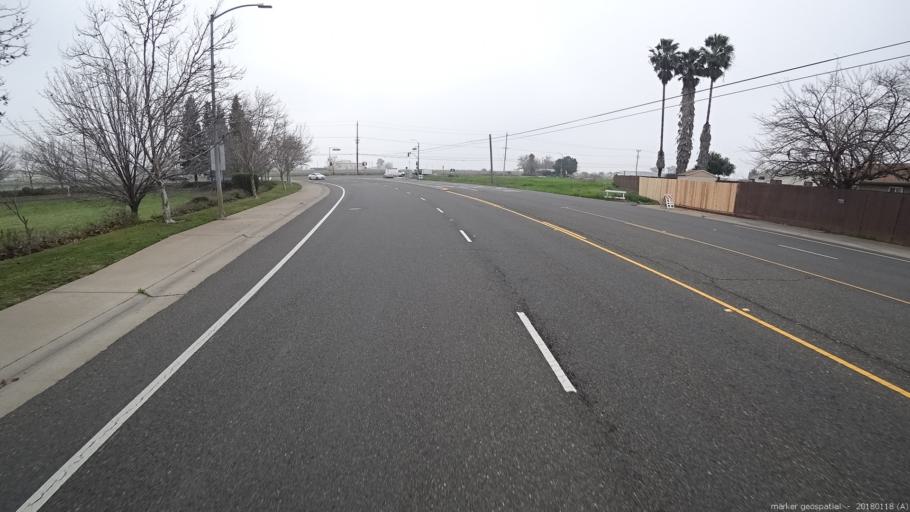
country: US
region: California
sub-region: Sacramento County
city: Rancho Cordova
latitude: 38.5620
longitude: -121.3179
